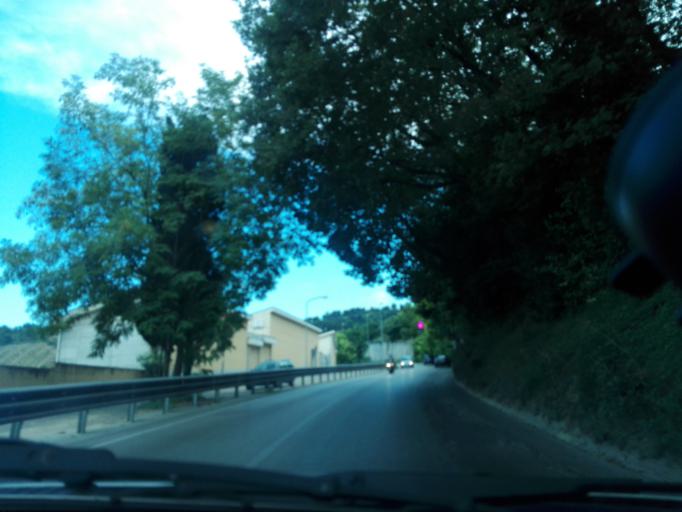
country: IT
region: Abruzzo
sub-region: Provincia di Pescara
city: Montesilvano Marina
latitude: 42.5000
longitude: 14.1405
